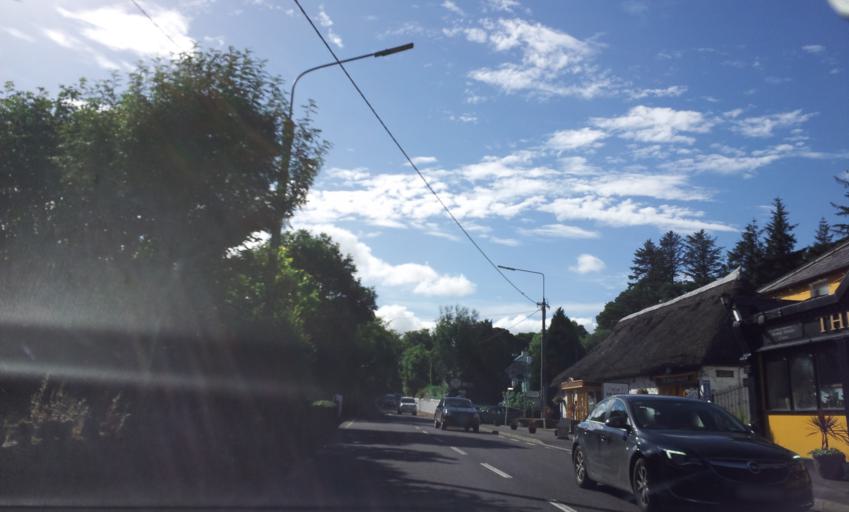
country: IE
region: Munster
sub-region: County Cork
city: Millstreet
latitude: 51.9455
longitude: -9.1702
